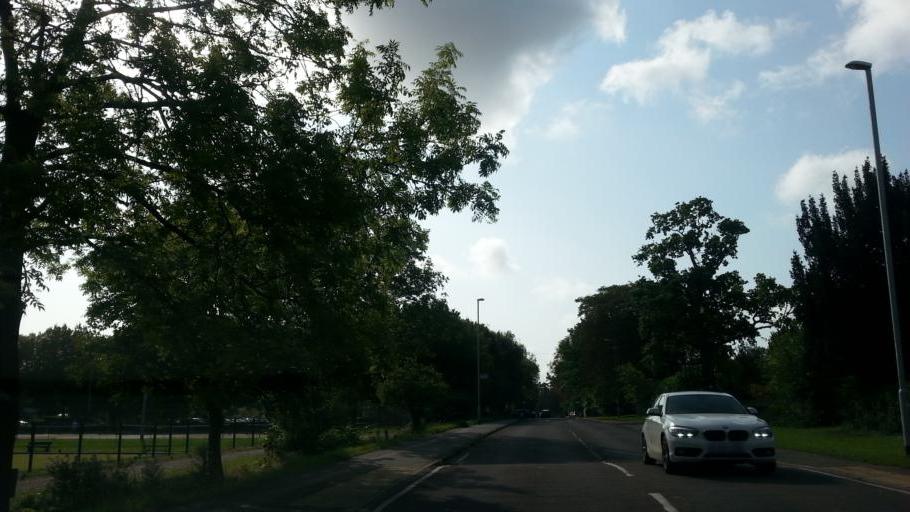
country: GB
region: England
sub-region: Cambridgeshire
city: Papworth Everard
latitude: 52.2527
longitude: -0.1203
